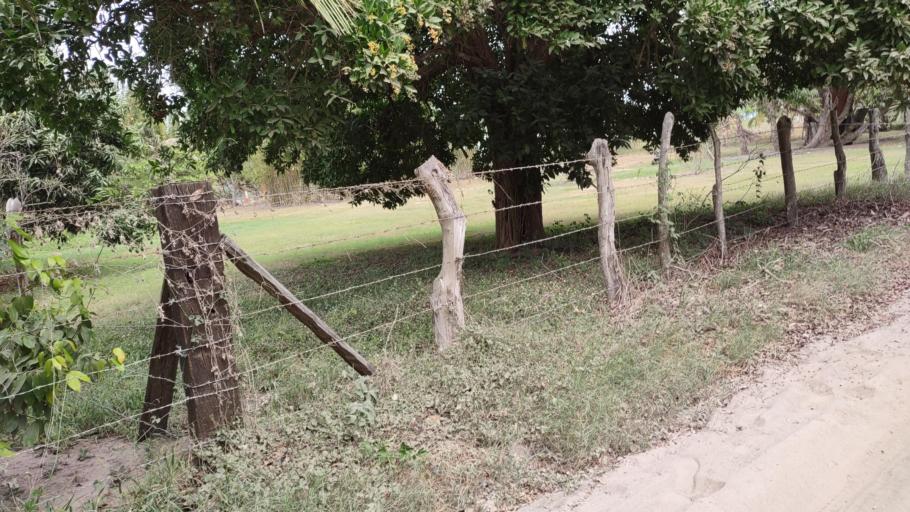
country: MX
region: Veracruz
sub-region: La Antigua
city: Nicolas Blanco (San Pancho)
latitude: 19.3102
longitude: -96.3026
